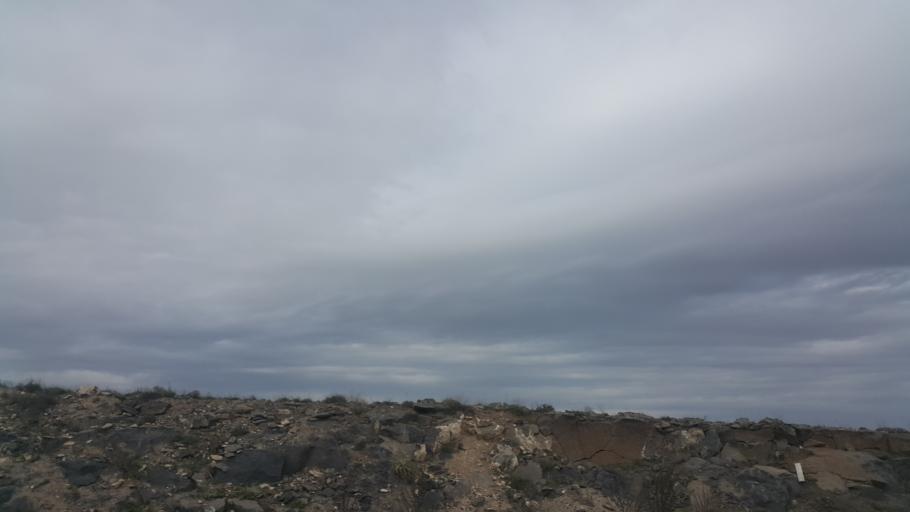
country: TR
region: Konya
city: Beyviran
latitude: 37.9245
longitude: 34.1104
